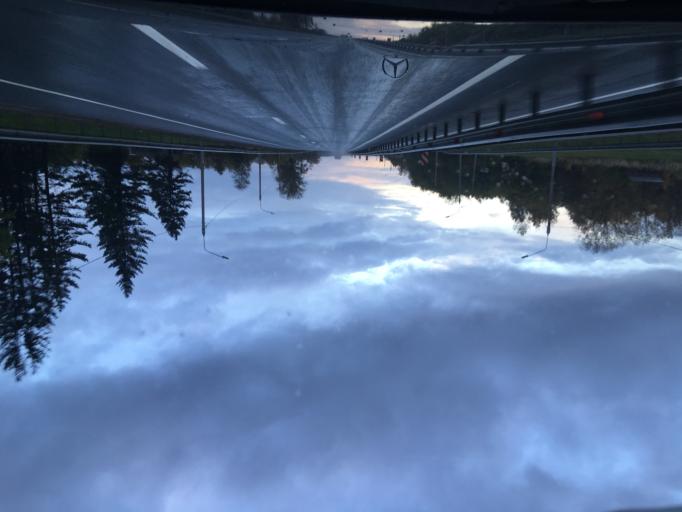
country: RU
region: Smolensk
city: Yartsevo
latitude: 55.0742
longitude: 32.6536
